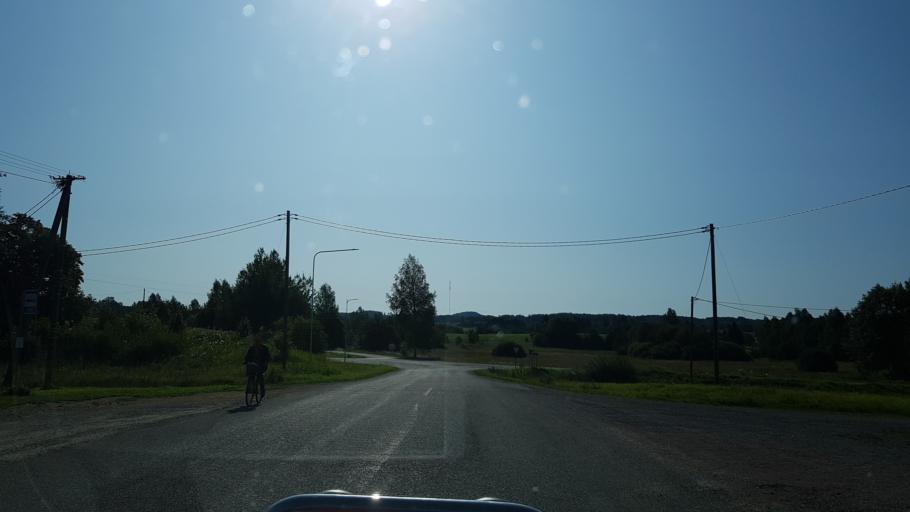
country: LV
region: Apes Novads
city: Ape
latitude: 57.6097
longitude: 26.8333
